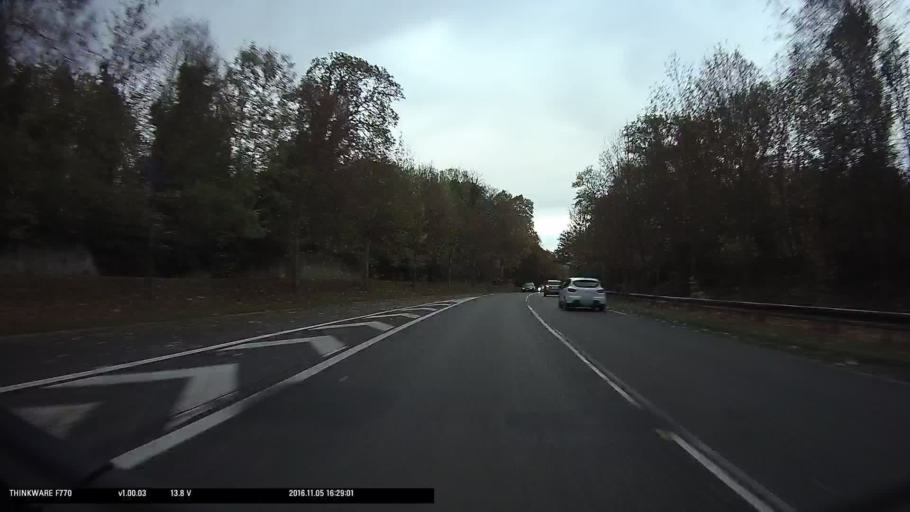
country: FR
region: Ile-de-France
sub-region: Departement du Val-d'Oise
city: Sagy
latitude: 49.0342
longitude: 1.9388
